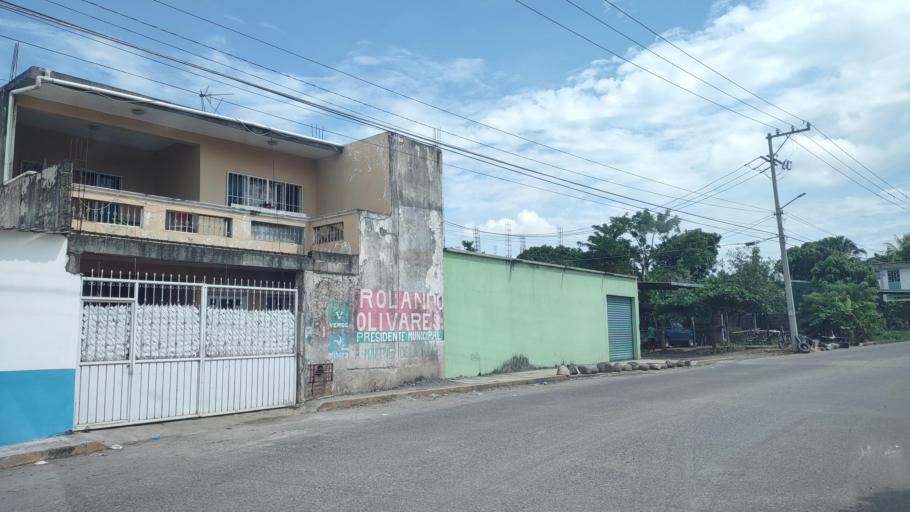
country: MX
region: Veracruz
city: Martinez de la Torre
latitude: 20.0707
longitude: -97.0743
